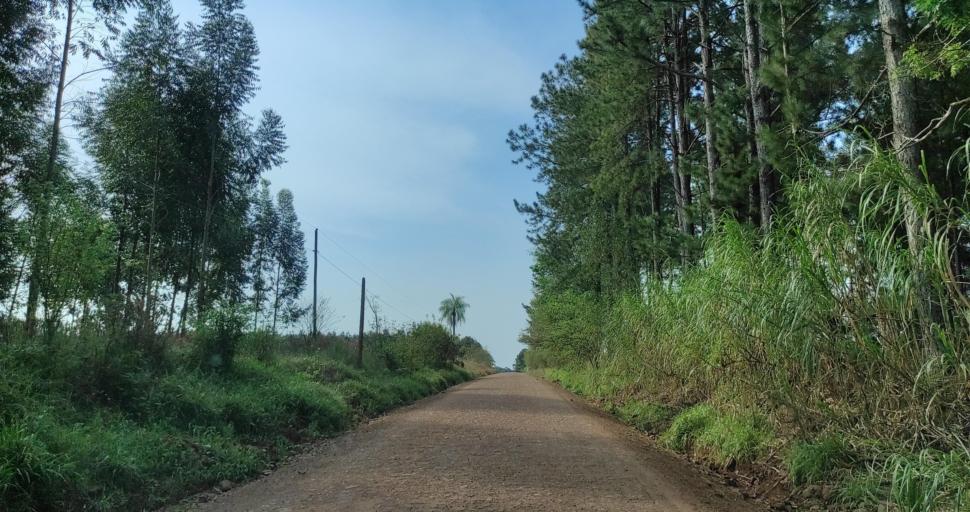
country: AR
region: Misiones
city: Garuhape
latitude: -26.8685
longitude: -55.0053
